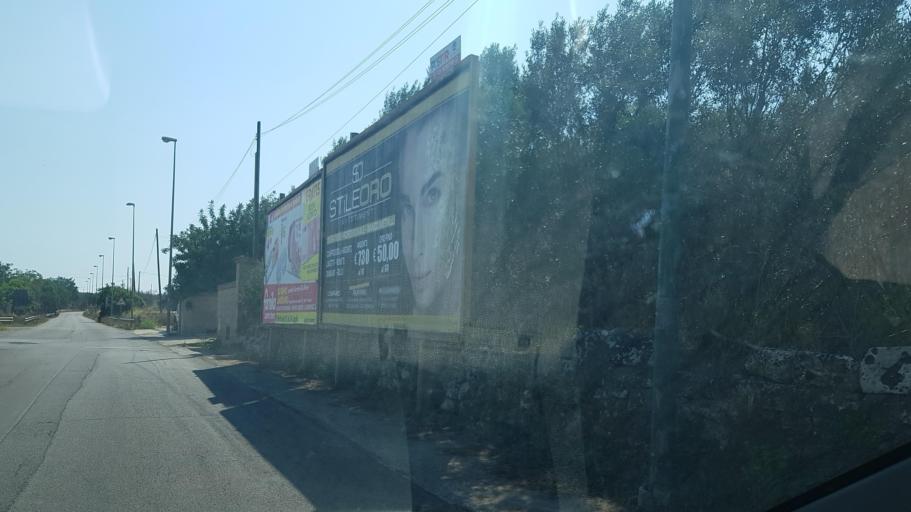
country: IT
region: Apulia
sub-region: Provincia di Lecce
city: Ruffano
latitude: 39.9872
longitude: 18.2603
